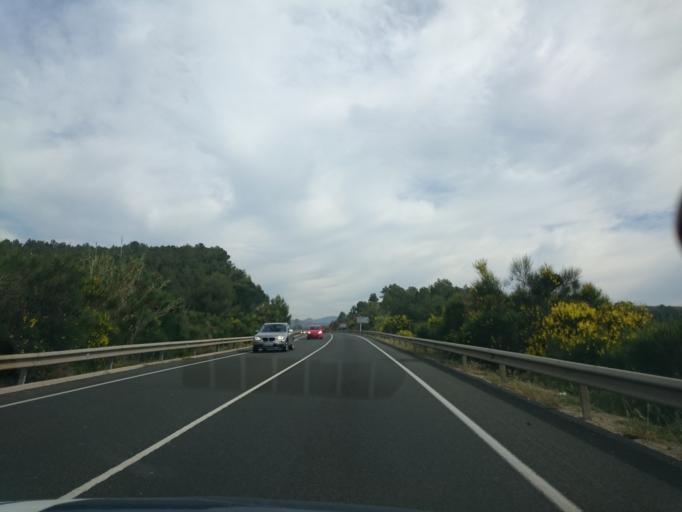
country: ES
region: Catalonia
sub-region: Provincia de Barcelona
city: Sant Pere de Riudebitlles
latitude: 41.4741
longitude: 1.6952
